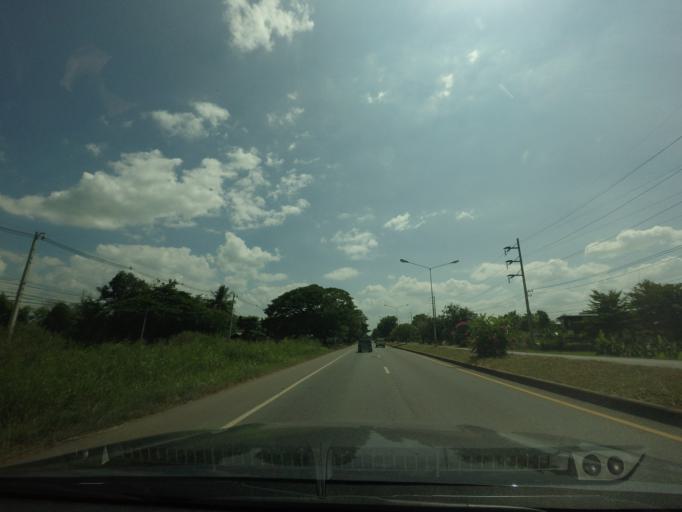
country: TH
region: Phetchabun
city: Nong Phai
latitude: 15.9324
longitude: 101.0267
